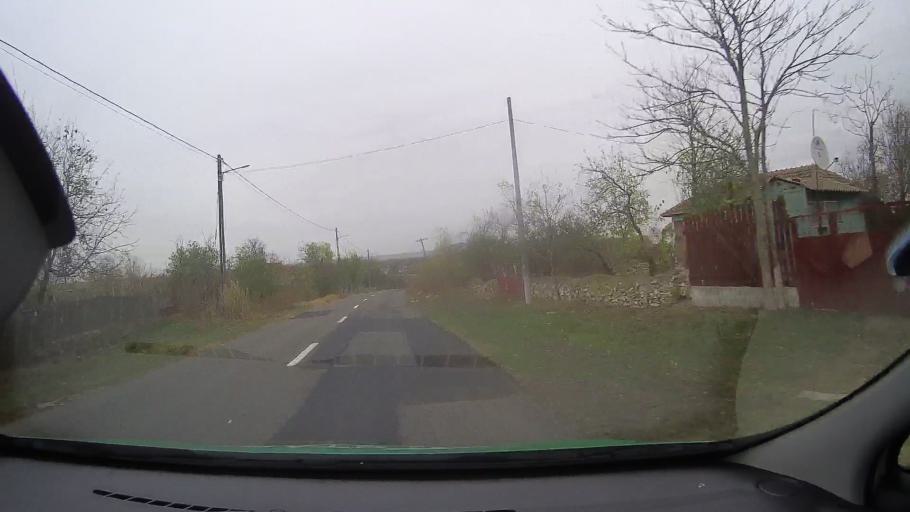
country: RO
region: Constanta
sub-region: Comuna Vulturu
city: Vulturu
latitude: 44.6979
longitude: 28.2411
